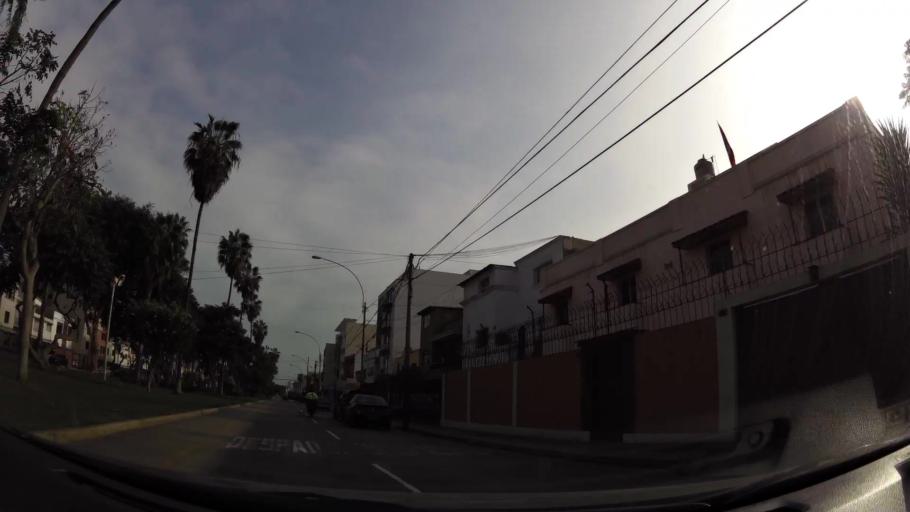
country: PE
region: Lima
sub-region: Lima
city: San Isidro
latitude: -12.0891
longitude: -77.0625
